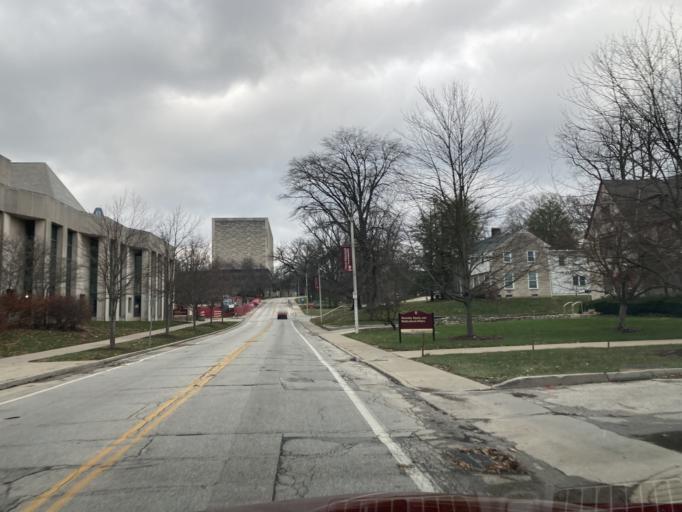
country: US
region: Indiana
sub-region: Monroe County
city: Bloomington
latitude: 39.1680
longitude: -86.5161
